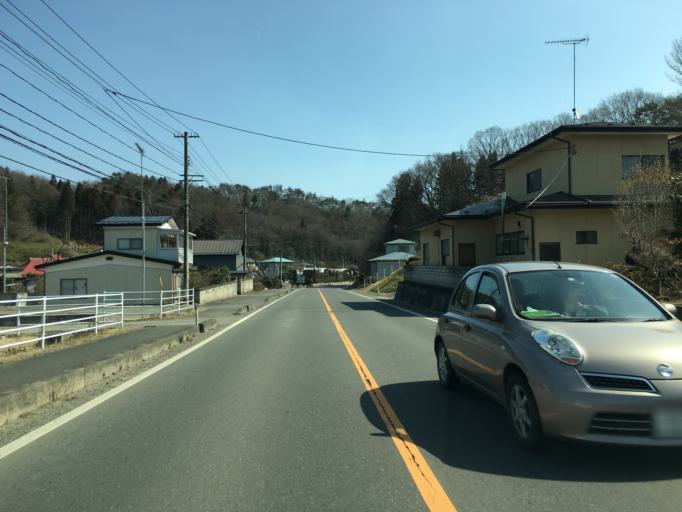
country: JP
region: Fukushima
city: Ishikawa
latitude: 37.1322
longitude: 140.2883
